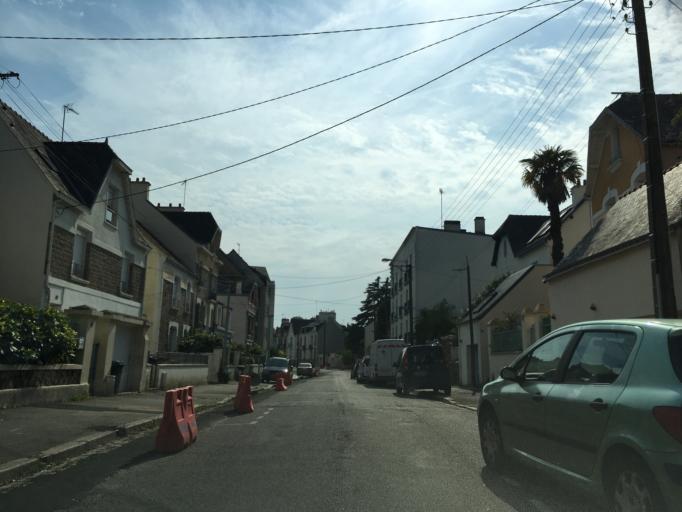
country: FR
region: Brittany
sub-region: Departement du Morbihan
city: Lorient
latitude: 47.7559
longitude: -3.3729
